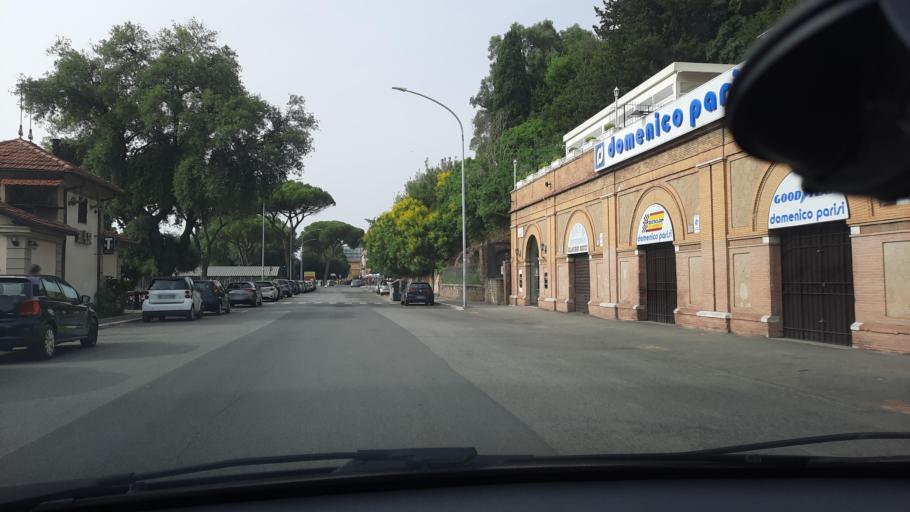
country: IT
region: Latium
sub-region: Citta metropolitana di Roma Capitale
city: Rome
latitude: 41.8588
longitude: 12.4781
